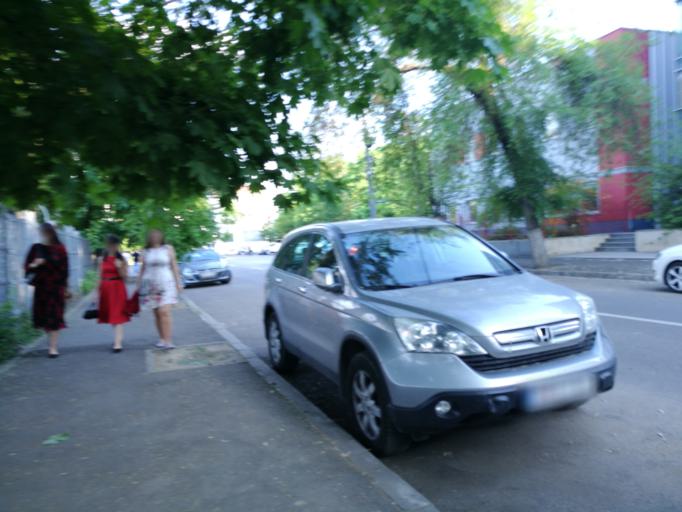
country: RO
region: Bucuresti
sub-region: Municipiul Bucuresti
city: Bucuresti
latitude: 44.4644
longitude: 26.0619
